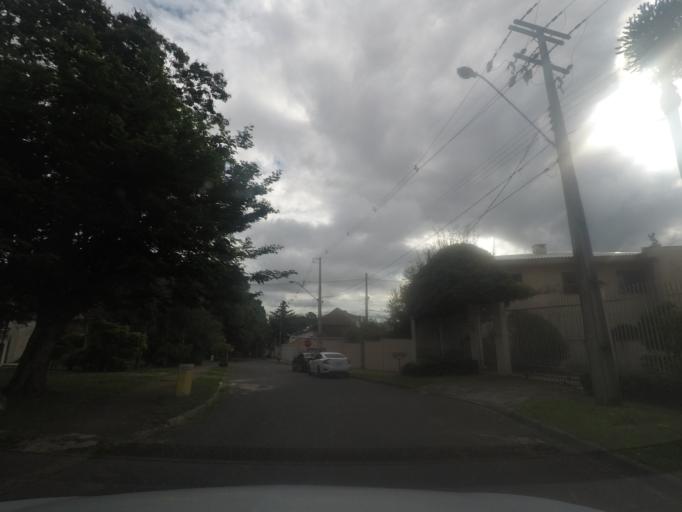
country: BR
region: Parana
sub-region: Curitiba
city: Curitiba
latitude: -25.4286
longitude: -49.2432
